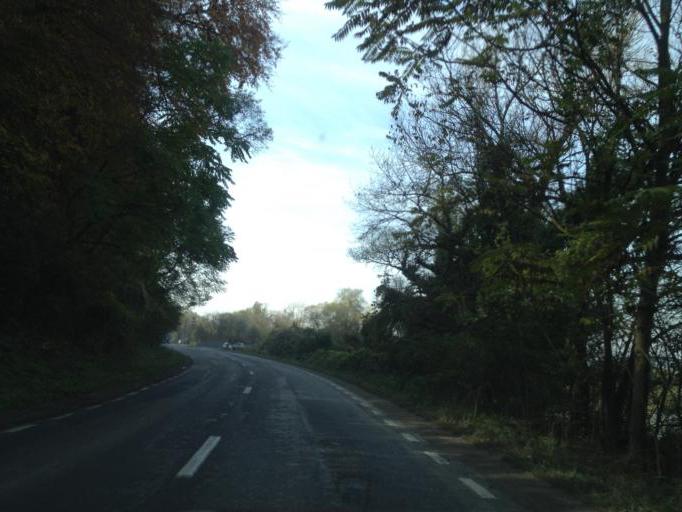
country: RO
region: Hunedoara
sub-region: Comuna Ilia
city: Ilia
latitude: 45.9215
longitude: 22.6657
